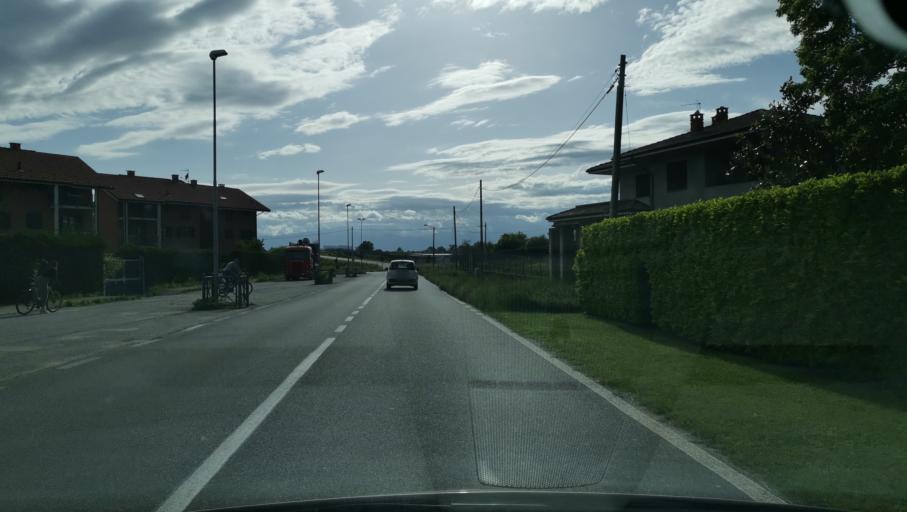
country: IT
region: Piedmont
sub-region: Provincia di Torino
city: Foglizzo
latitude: 45.2754
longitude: 7.8175
